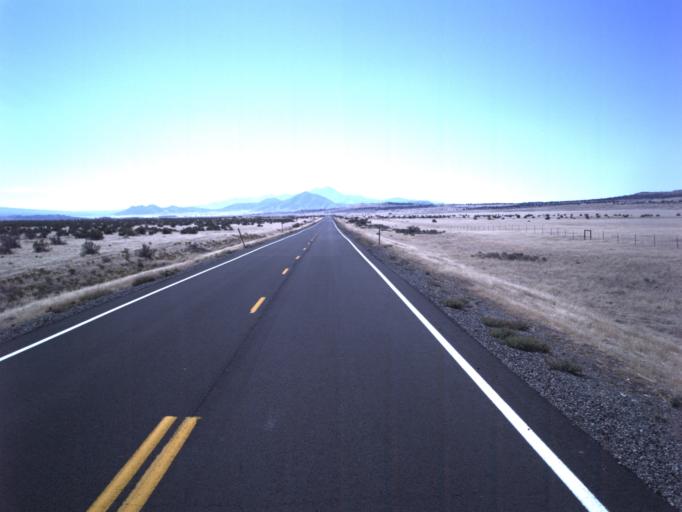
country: US
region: Utah
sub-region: Tooele County
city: Grantsville
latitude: 40.2848
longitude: -112.7420
